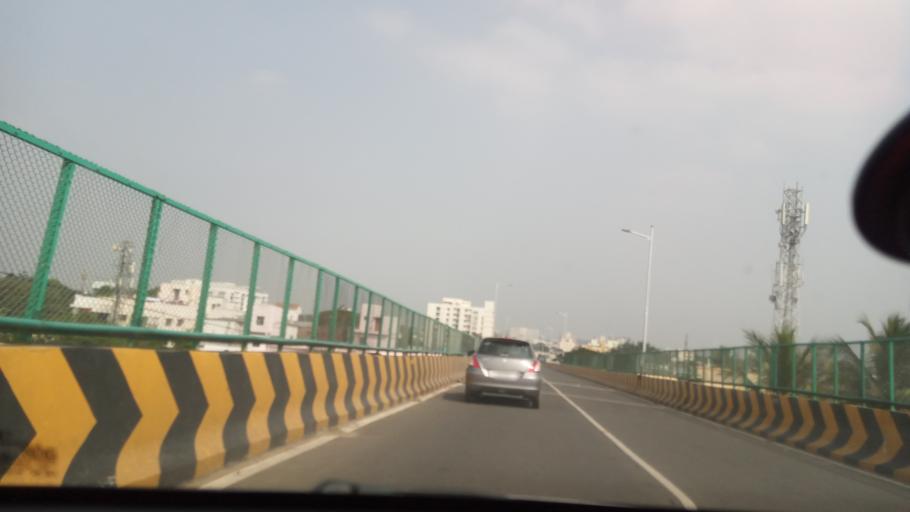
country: IN
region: Tamil Nadu
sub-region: Coimbatore
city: Coimbatore
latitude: 11.0211
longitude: 76.9733
